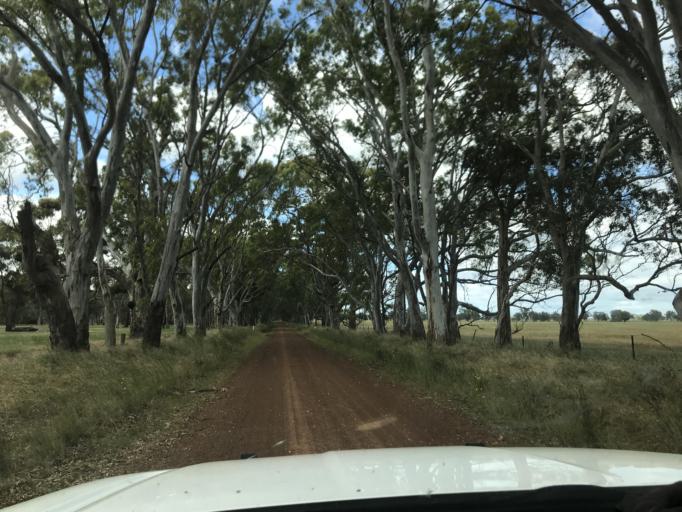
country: AU
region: South Australia
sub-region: Naracoorte and Lucindale
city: Naracoorte
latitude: -37.0278
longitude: 141.2599
